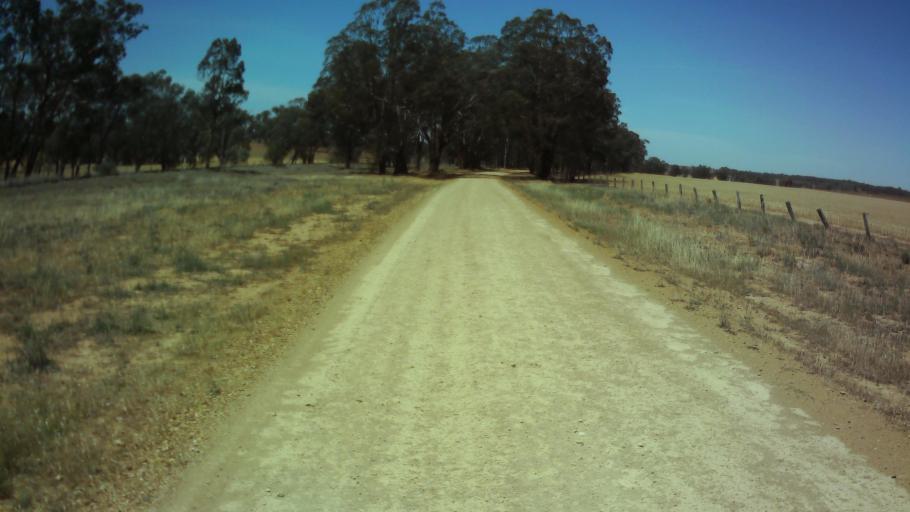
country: AU
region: New South Wales
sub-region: Weddin
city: Grenfell
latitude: -33.9210
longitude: 148.1966
